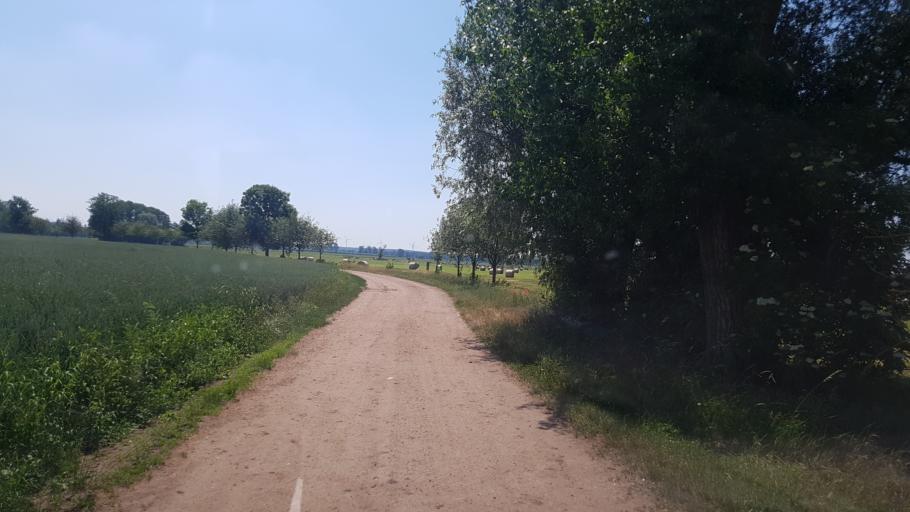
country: DE
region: Brandenburg
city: Schlieben
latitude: 51.7233
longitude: 13.3266
